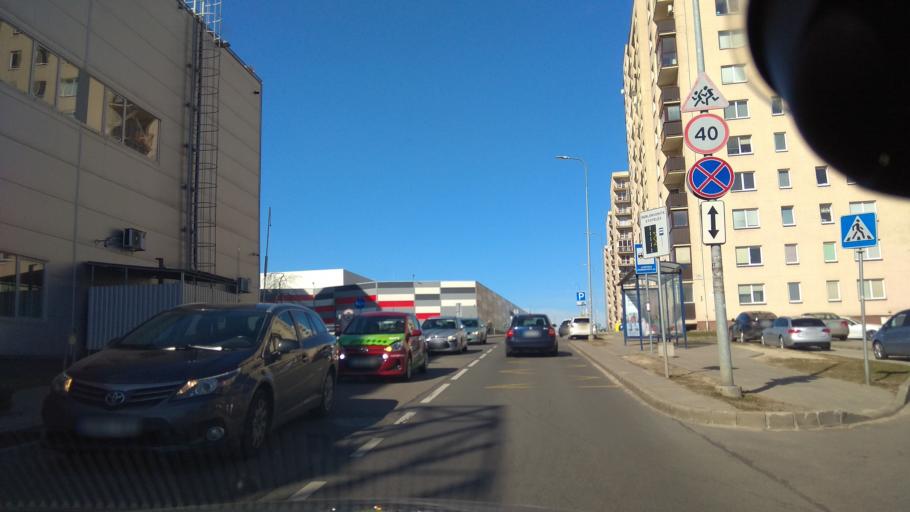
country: LT
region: Vilnius County
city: Pasilaiciai
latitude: 54.7409
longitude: 25.2292
